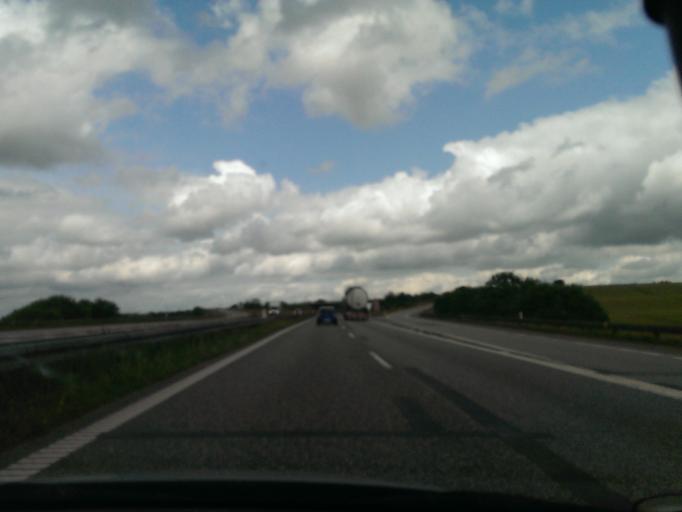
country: DK
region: North Denmark
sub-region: Mariagerfjord Kommune
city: Hobro
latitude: 56.5878
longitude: 9.7769
